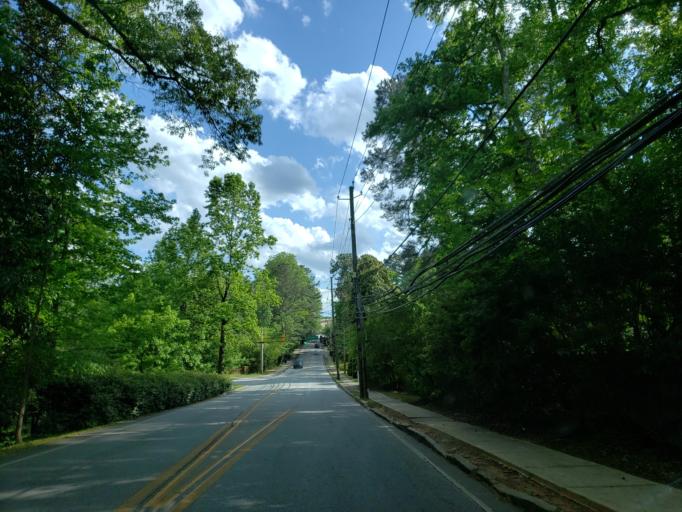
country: US
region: Georgia
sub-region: DeKalb County
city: North Druid Hills
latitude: 33.8500
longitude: -84.2832
